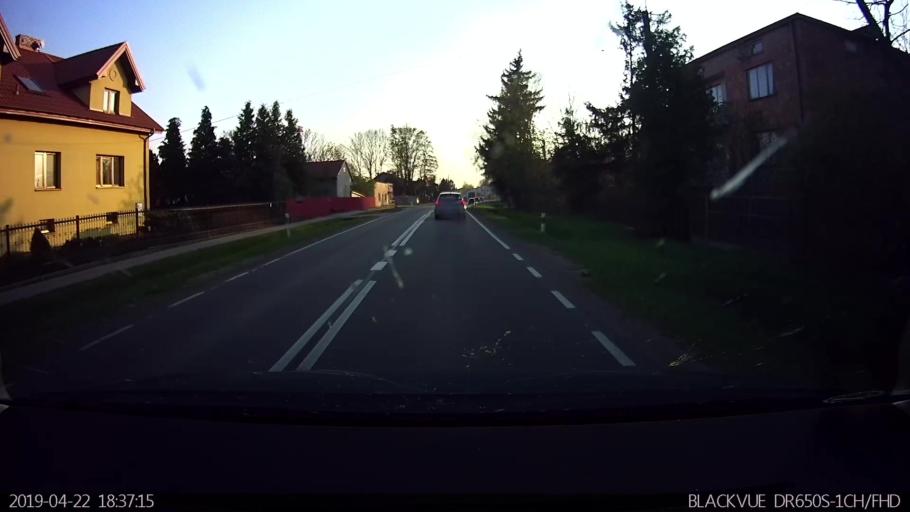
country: PL
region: Masovian Voivodeship
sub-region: Powiat wolominski
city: Klembow
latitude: 52.4433
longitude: 21.3125
